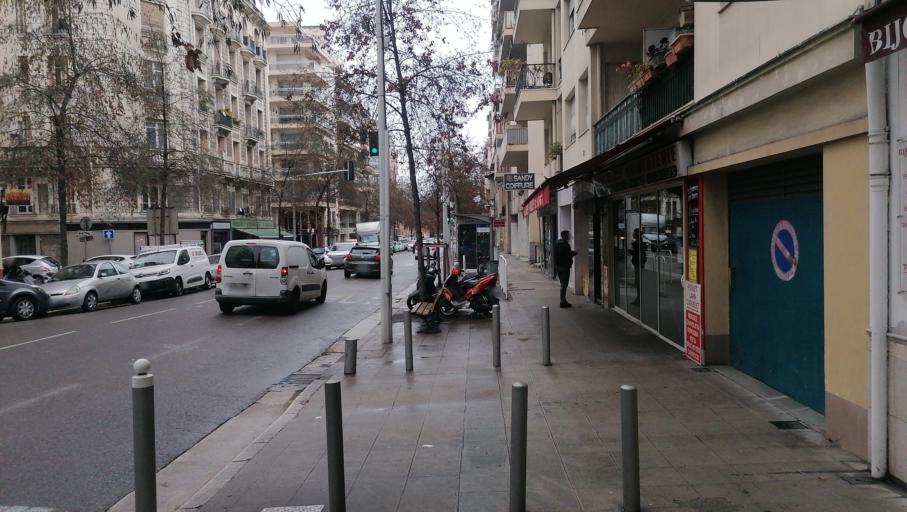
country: FR
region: Provence-Alpes-Cote d'Azur
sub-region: Departement des Alpes-Maritimes
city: Nice
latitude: 43.7176
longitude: 7.2529
